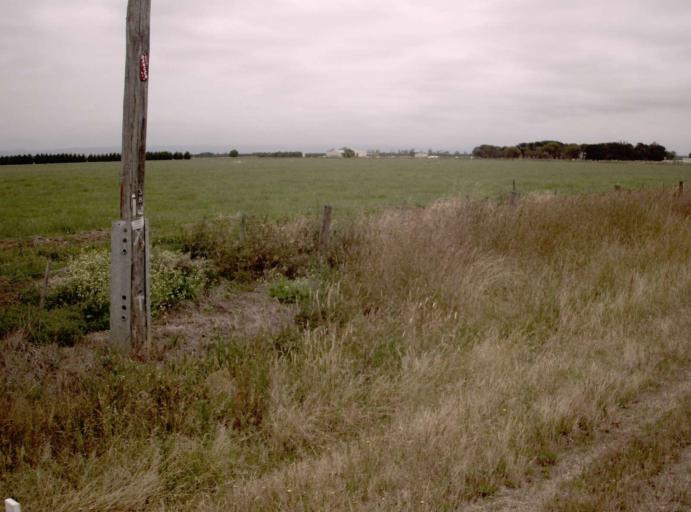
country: AU
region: Victoria
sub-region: Wellington
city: Heyfield
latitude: -38.0832
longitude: 146.7715
